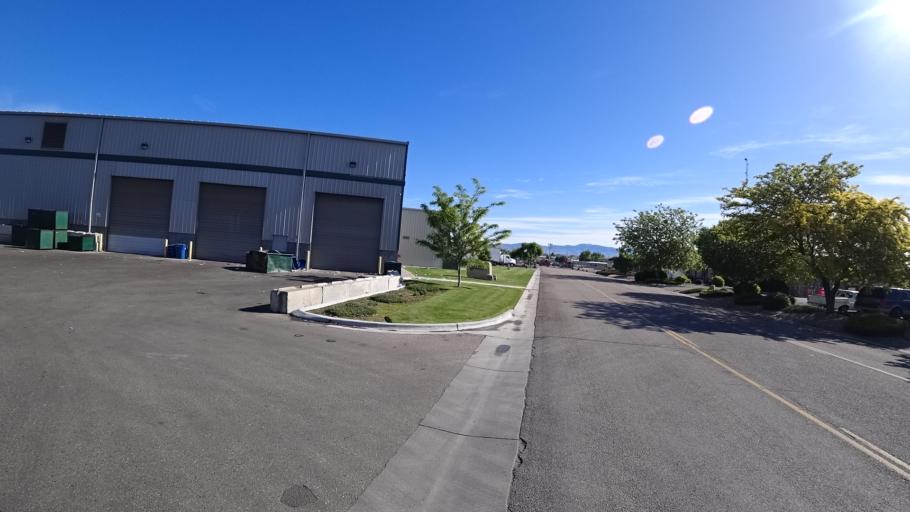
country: US
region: Idaho
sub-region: Ada County
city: Garden City
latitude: 43.5853
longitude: -116.2713
